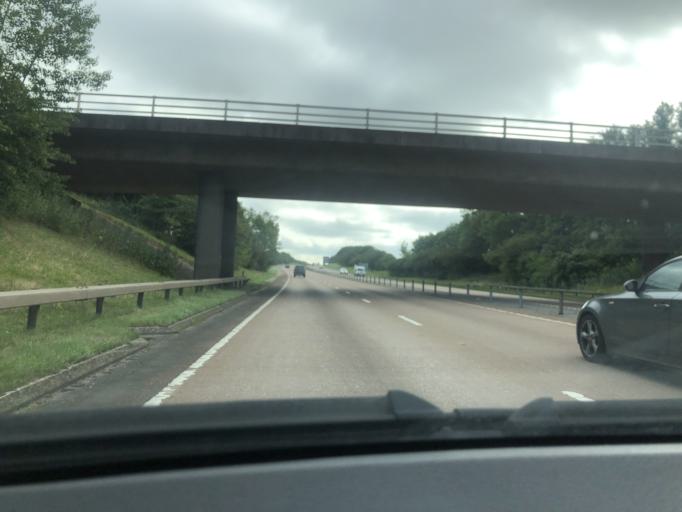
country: GB
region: England
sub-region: Devon
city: Topsham
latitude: 50.7295
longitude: -3.4310
